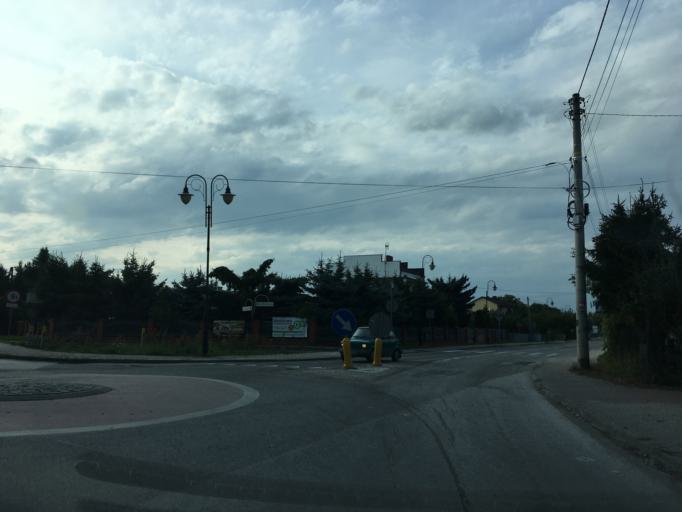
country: PL
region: Swietokrzyskie
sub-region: Powiat wloszczowski
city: Wloszczowa
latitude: 50.8480
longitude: 19.9921
